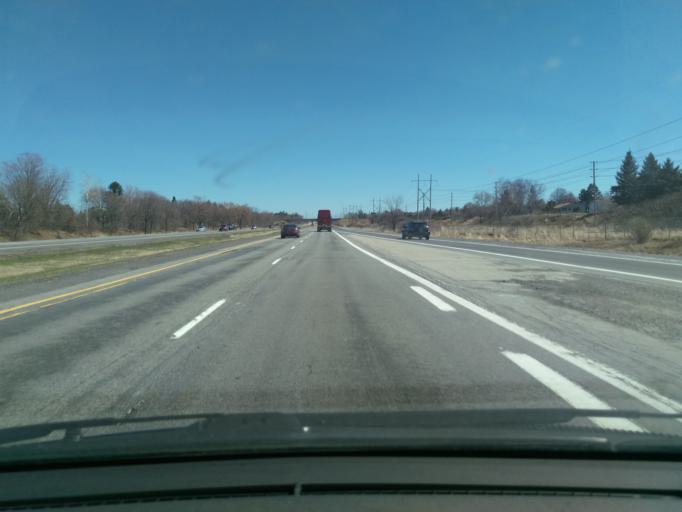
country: CA
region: Quebec
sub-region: Outaouais
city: Gatineau
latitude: 45.4704
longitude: -75.5420
